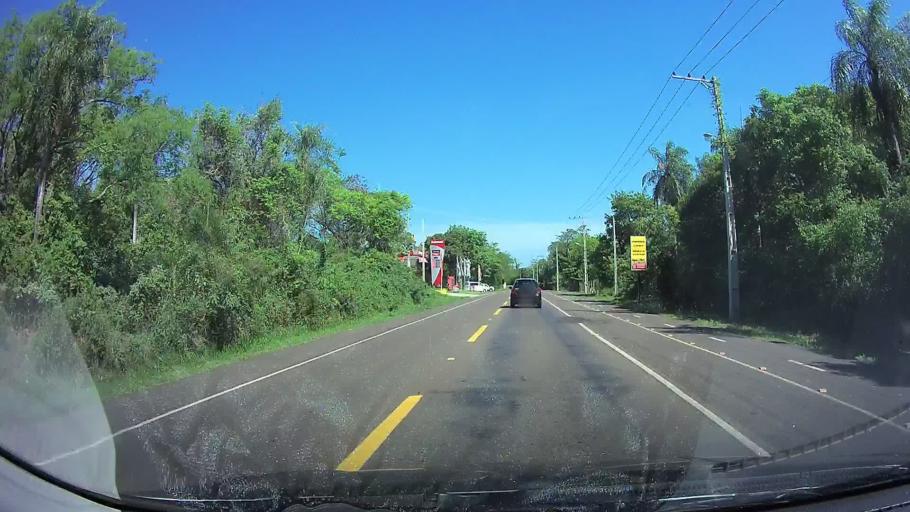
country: PY
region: Cordillera
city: San Bernardino
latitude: -25.2477
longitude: -57.3225
